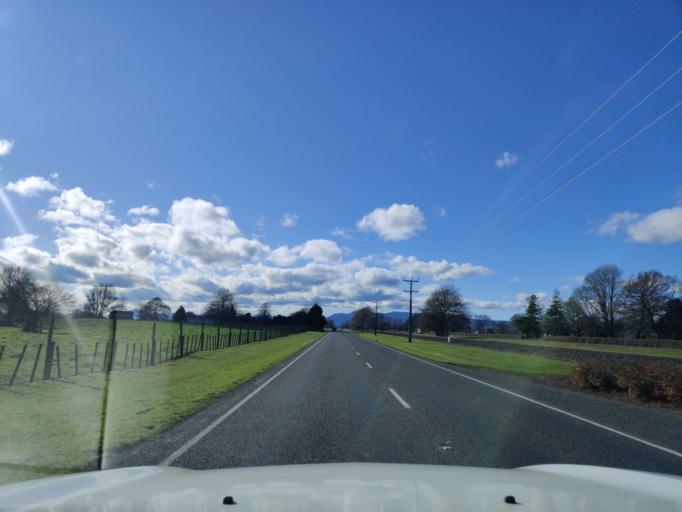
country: NZ
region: Waikato
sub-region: Matamata-Piako District
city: Matamata
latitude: -37.8481
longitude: 175.7602
